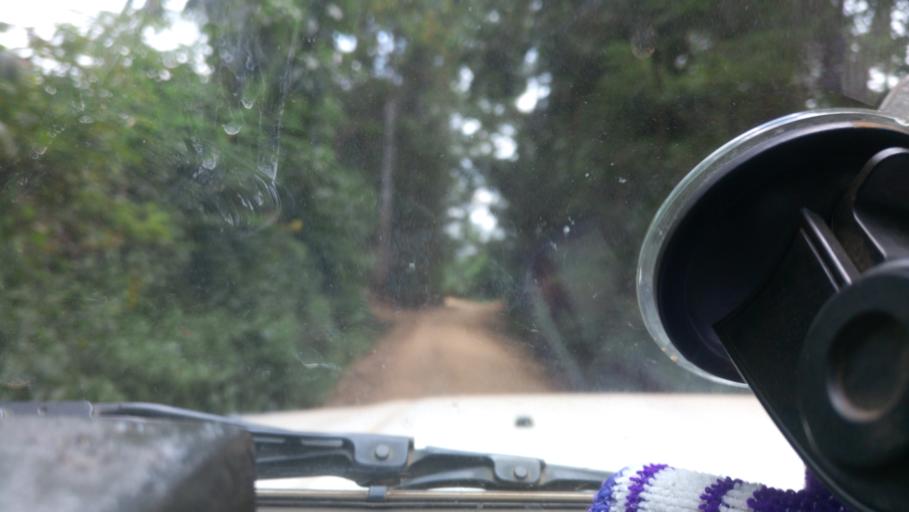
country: KE
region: Kericho
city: Litein
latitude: -0.6081
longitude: 35.1362
